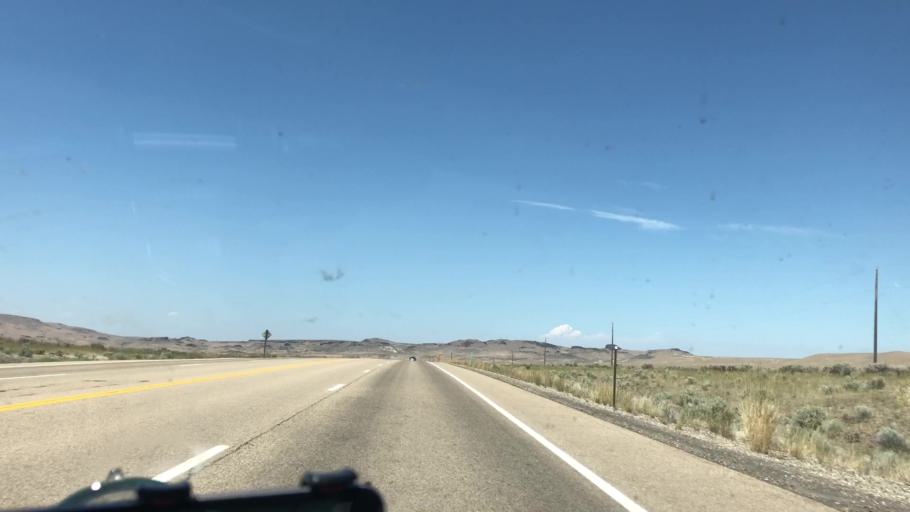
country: US
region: Idaho
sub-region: Owyhee County
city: Marsing
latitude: 43.2965
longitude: -116.9851
